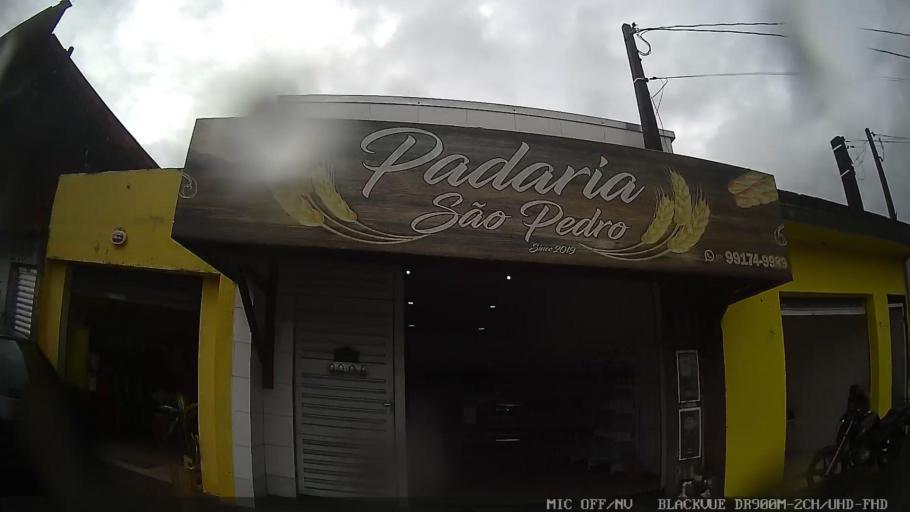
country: BR
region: Sao Paulo
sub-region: Itanhaem
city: Itanhaem
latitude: -24.1654
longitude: -46.7896
